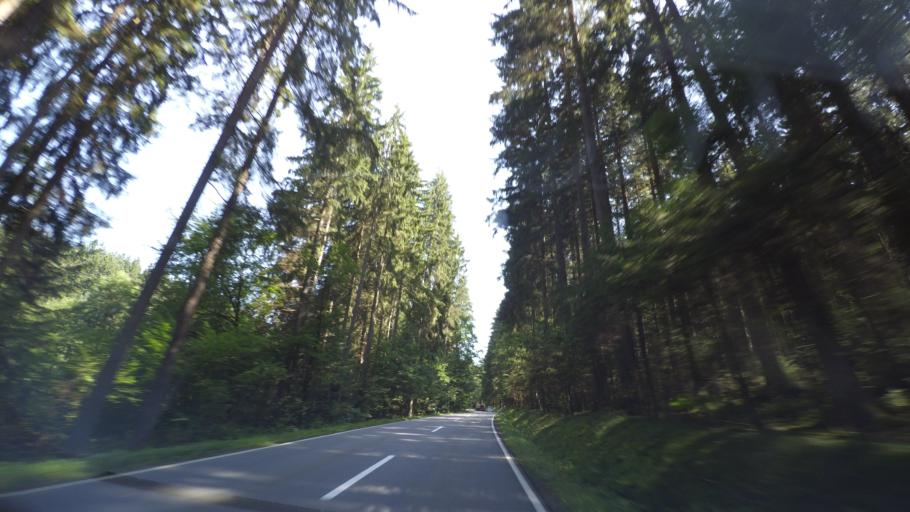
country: DE
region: Bavaria
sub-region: Lower Bavaria
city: Drachselsried
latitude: 49.0859
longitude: 12.9962
